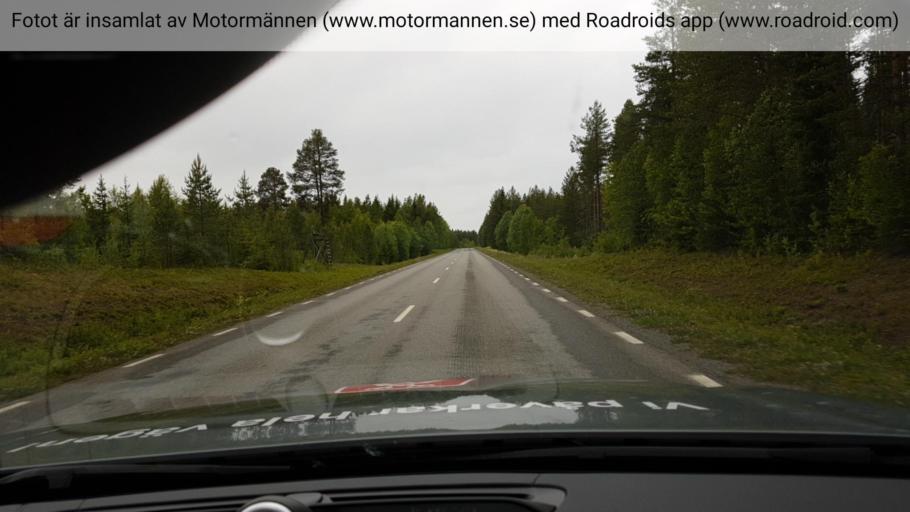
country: SE
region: Jaemtland
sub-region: Stroemsunds Kommun
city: Stroemsund
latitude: 63.6018
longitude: 15.3036
